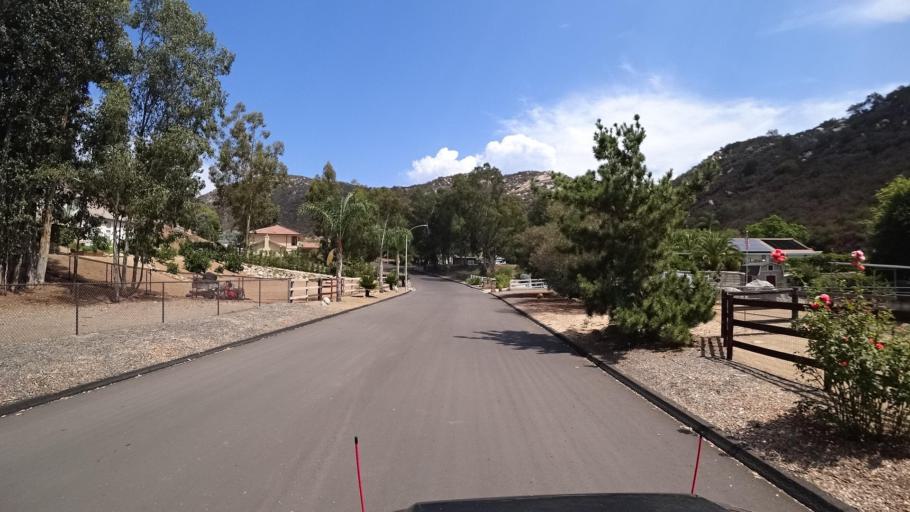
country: US
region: California
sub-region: San Diego County
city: Hidden Meadows
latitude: 33.1821
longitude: -117.0795
